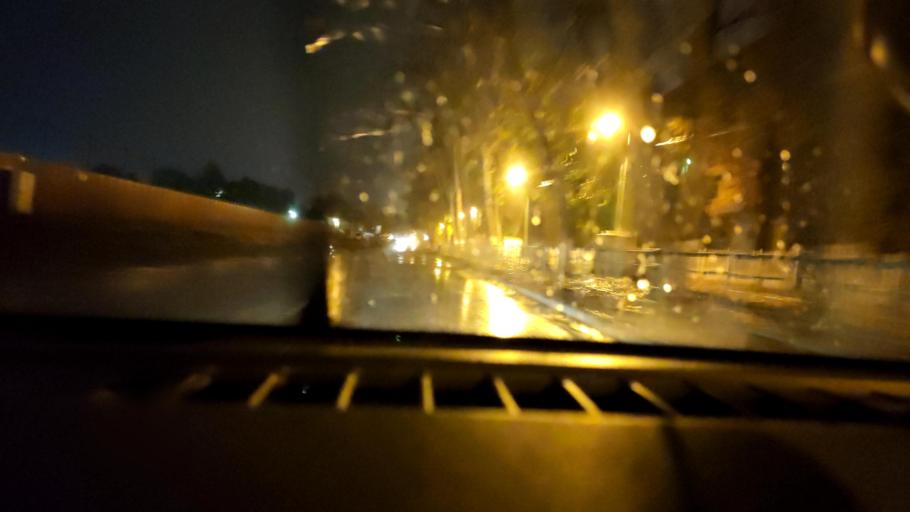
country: RU
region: Samara
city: Samara
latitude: 53.2069
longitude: 50.2460
